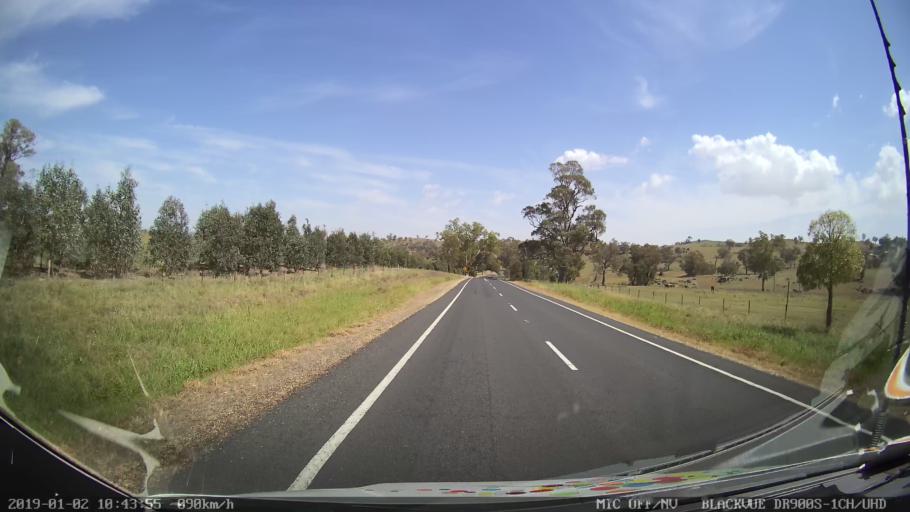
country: AU
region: New South Wales
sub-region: Cootamundra
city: Cootamundra
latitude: -34.7666
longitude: 148.3004
